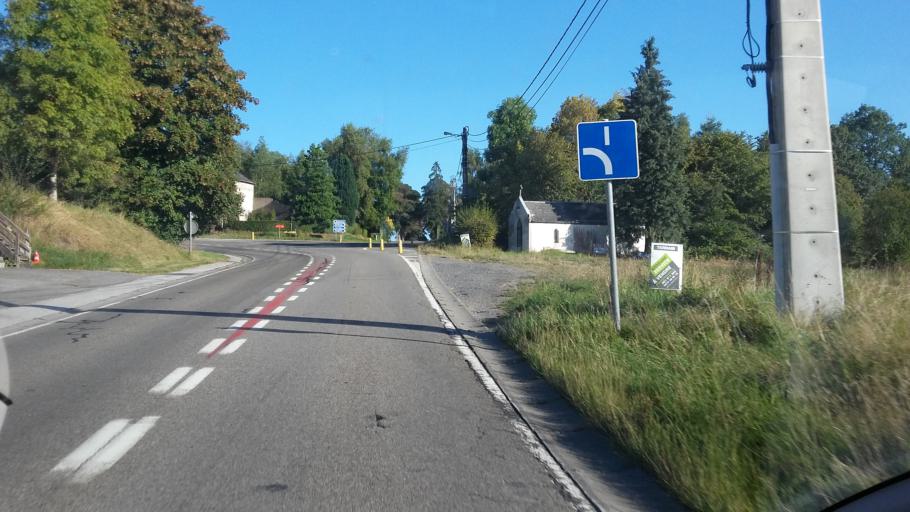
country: BE
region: Wallonia
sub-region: Province du Luxembourg
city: Neufchateau
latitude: 49.8348
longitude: 5.4774
